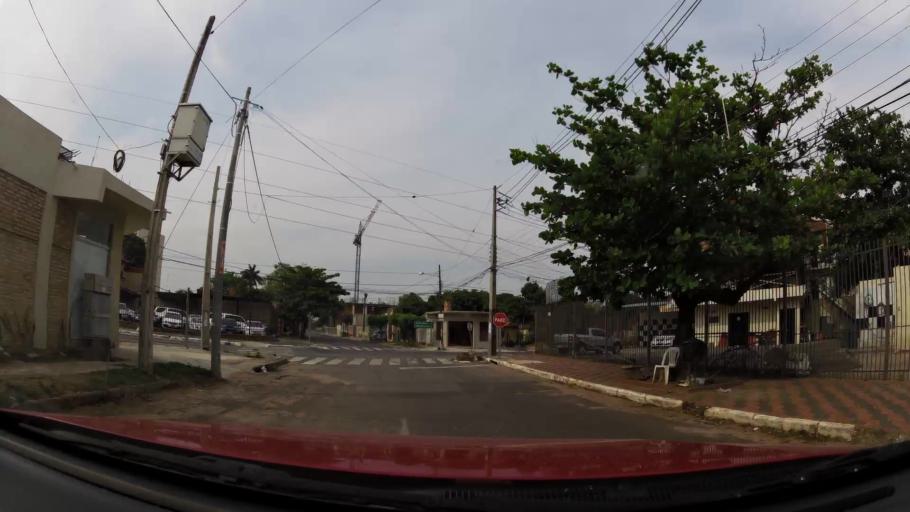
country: PY
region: Central
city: Fernando de la Mora
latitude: -25.2935
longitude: -57.5522
